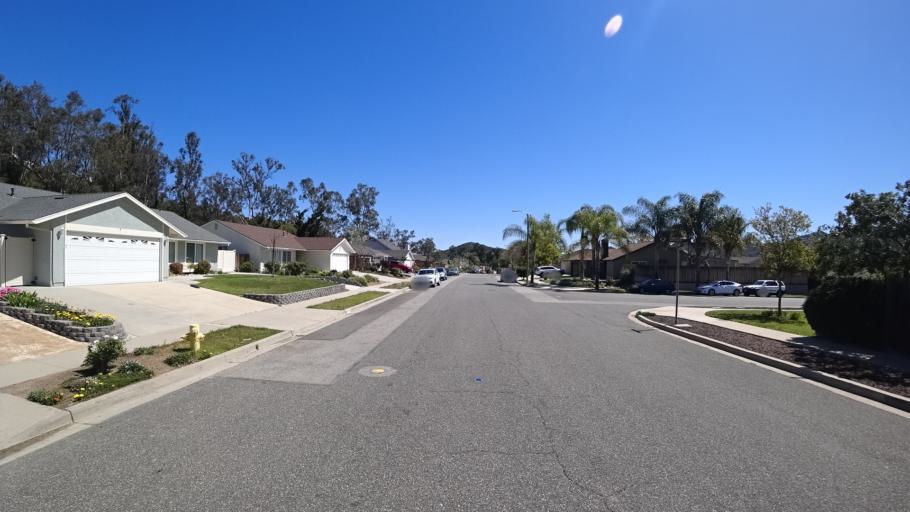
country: US
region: California
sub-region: Ventura County
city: Casa Conejo
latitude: 34.1608
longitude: -118.9642
